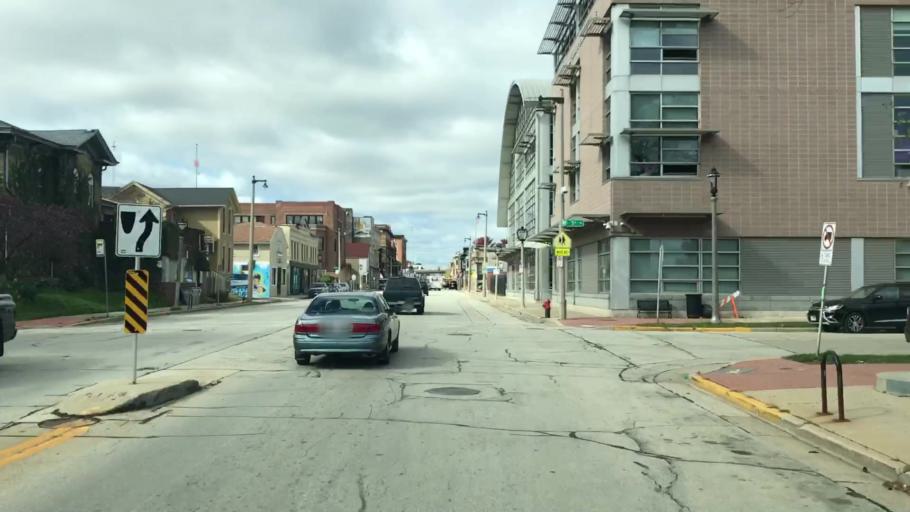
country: US
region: Wisconsin
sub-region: Milwaukee County
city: Milwaukee
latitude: 43.0233
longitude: -87.9138
